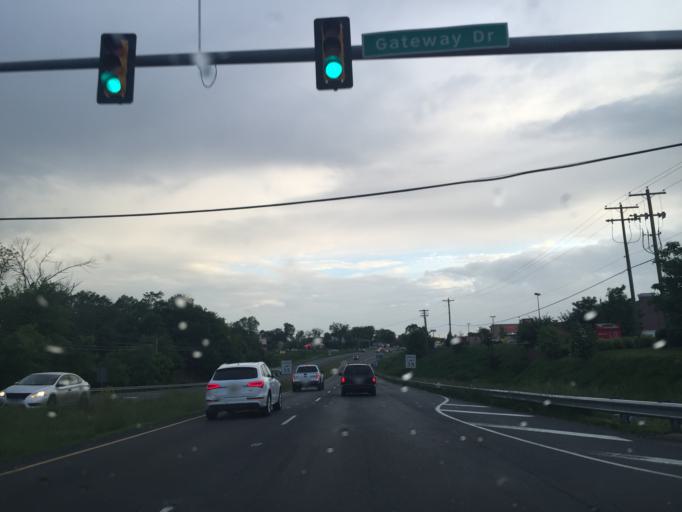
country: US
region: Virginia
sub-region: City of Winchester
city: Winchester
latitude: 39.1861
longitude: -78.1301
